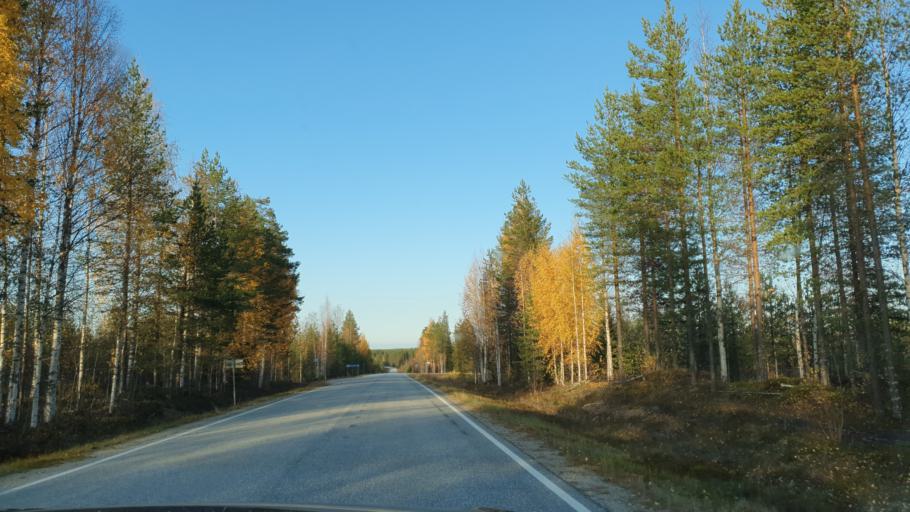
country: FI
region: Kainuu
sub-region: Kehys-Kainuu
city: Kuhmo
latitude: 64.4184
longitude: 29.4894
